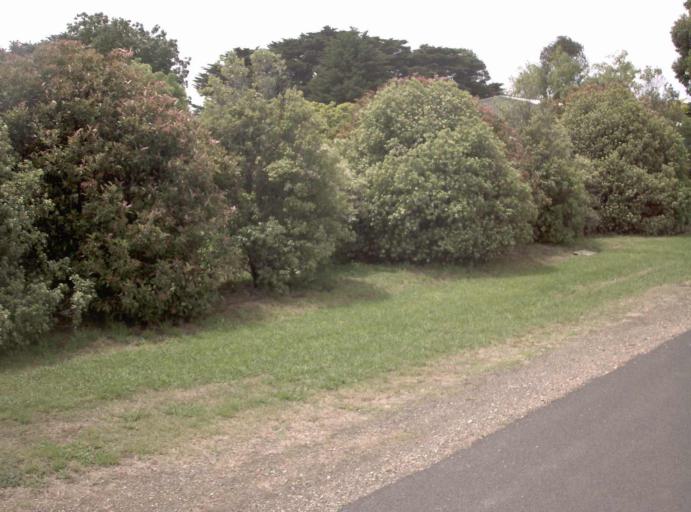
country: AU
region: Victoria
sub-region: Wellington
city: Sale
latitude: -38.0553
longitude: 147.0252
